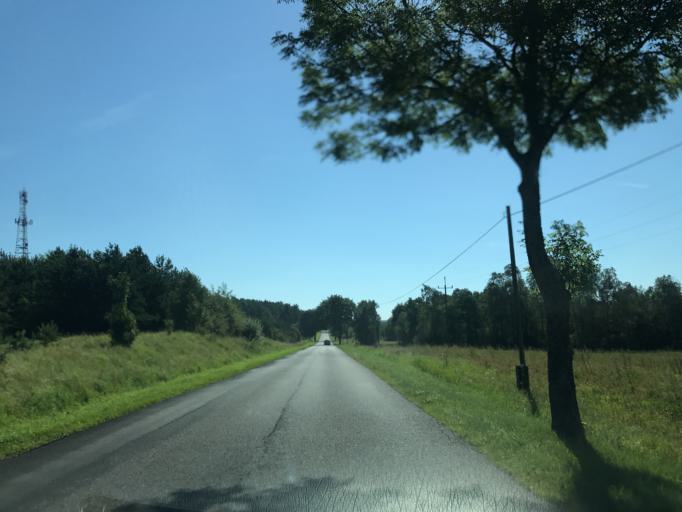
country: PL
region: Pomeranian Voivodeship
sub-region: Powiat bytowski
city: Czarna Dabrowka
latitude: 54.3597
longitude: 17.5408
